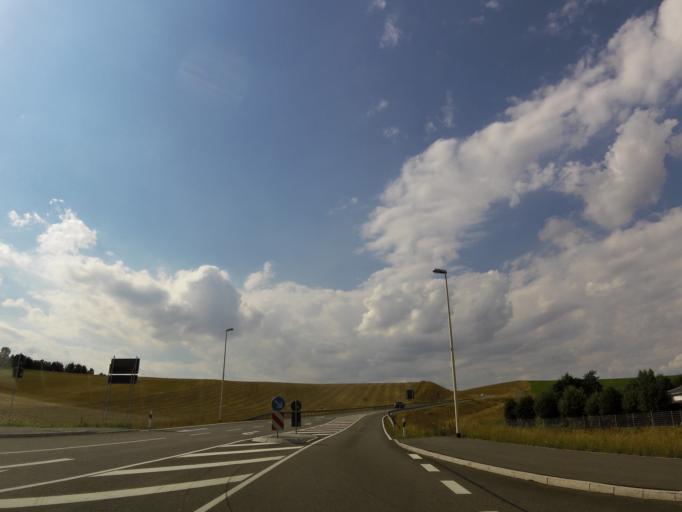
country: DE
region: Saxony
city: Pfaffroda
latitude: 50.8340
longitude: 12.5183
